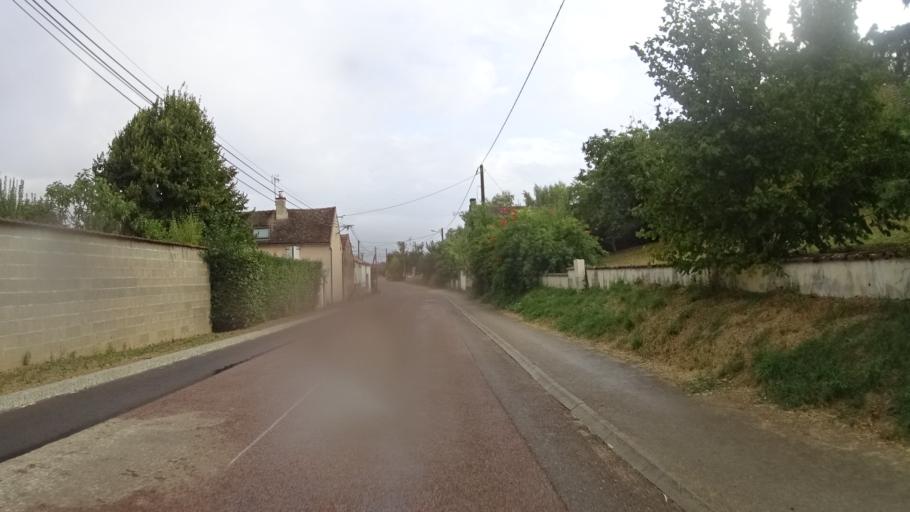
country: FR
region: Bourgogne
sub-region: Departement de Saone-et-Loire
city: Verdun-sur-le-Doubs
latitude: 46.9595
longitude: 5.0272
